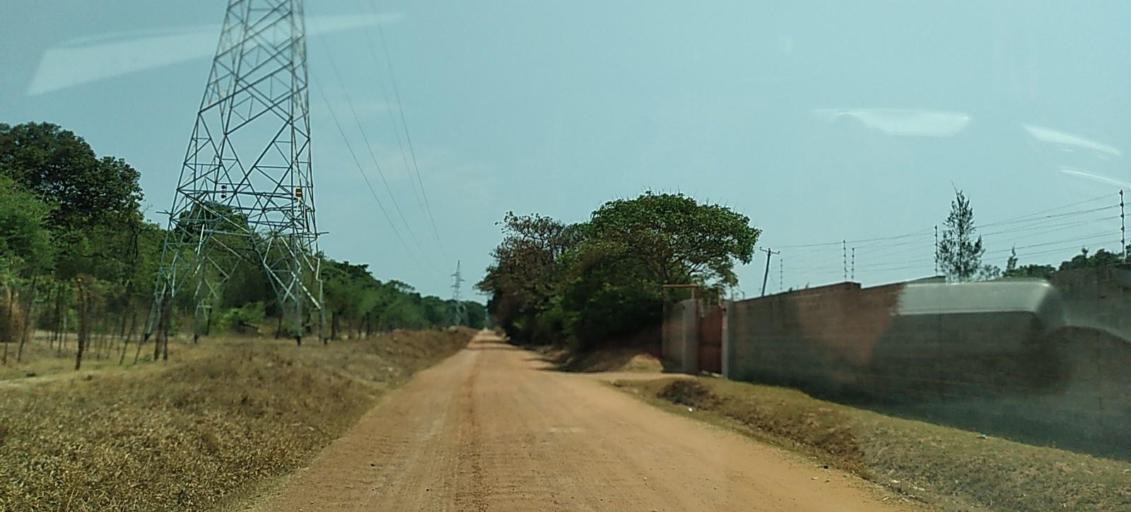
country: ZM
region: Copperbelt
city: Chambishi
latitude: -12.6147
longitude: 27.9508
